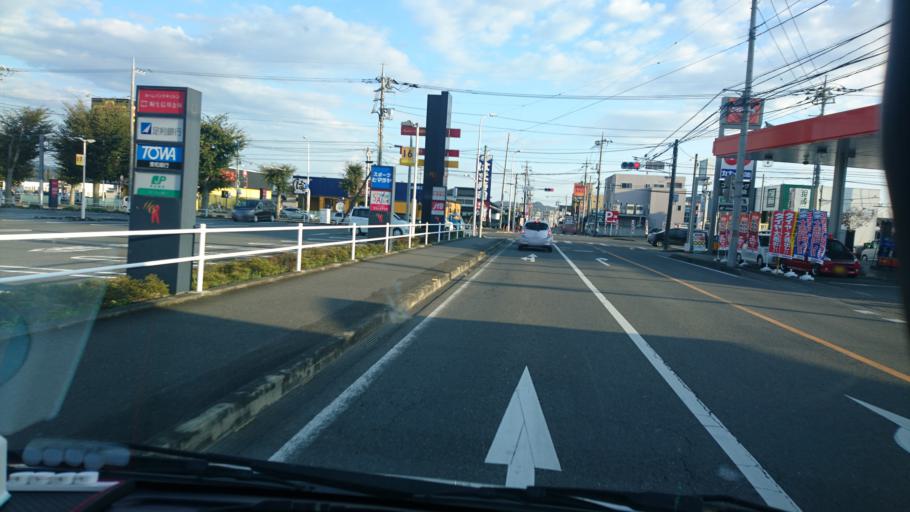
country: JP
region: Gunma
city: Kiryu
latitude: 36.4045
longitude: 139.3173
